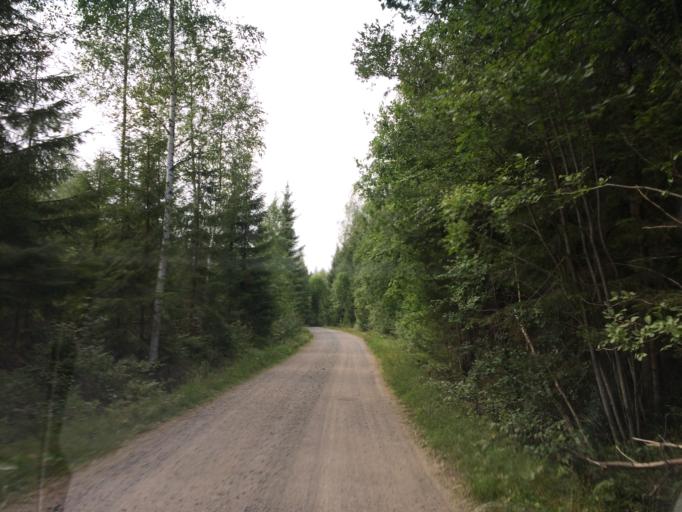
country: FI
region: Haeme
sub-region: Haemeenlinna
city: Hauho
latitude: 61.0750
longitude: 24.6488
